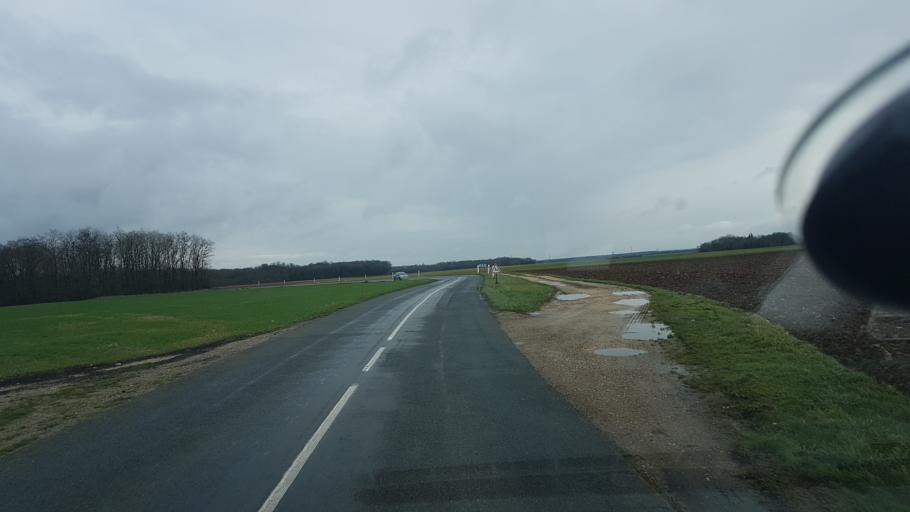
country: FR
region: Ile-de-France
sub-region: Departement de Seine-et-Marne
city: Souppes-sur-Loing
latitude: 48.2275
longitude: 2.8035
